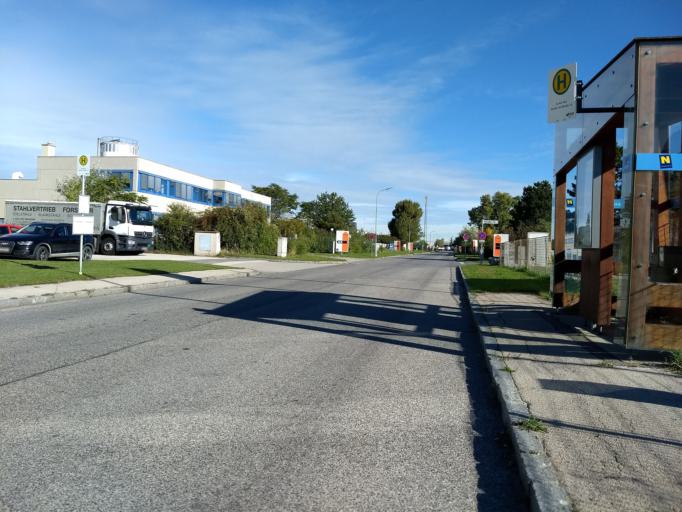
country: AT
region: Lower Austria
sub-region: Politischer Bezirk Modling
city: Neu-Guntramsdorf
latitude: 48.0644
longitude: 16.3290
